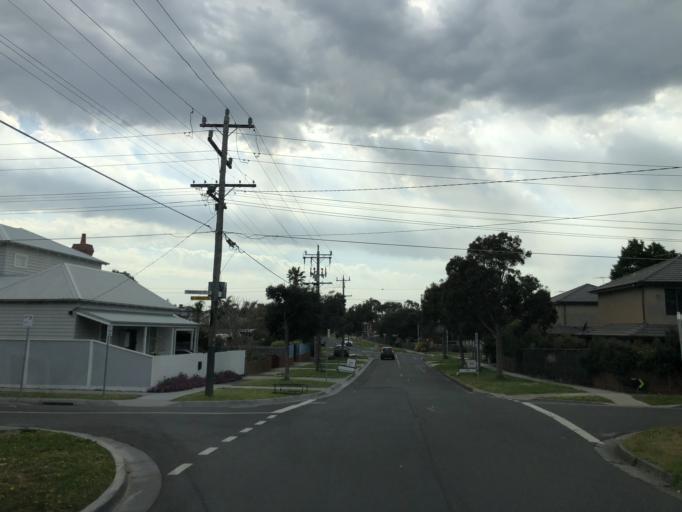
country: AU
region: Victoria
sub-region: Kingston
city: Carrum
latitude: -38.0782
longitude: 145.1246
